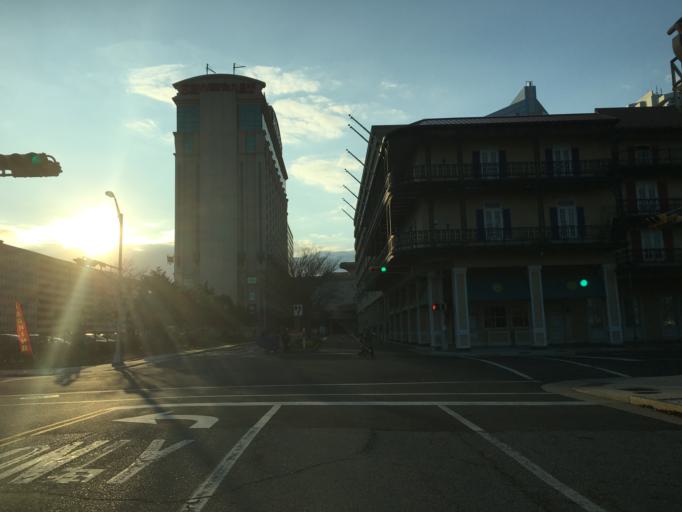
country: US
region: New Jersey
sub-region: Atlantic County
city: Atlantic City
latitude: 39.3639
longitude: -74.4195
